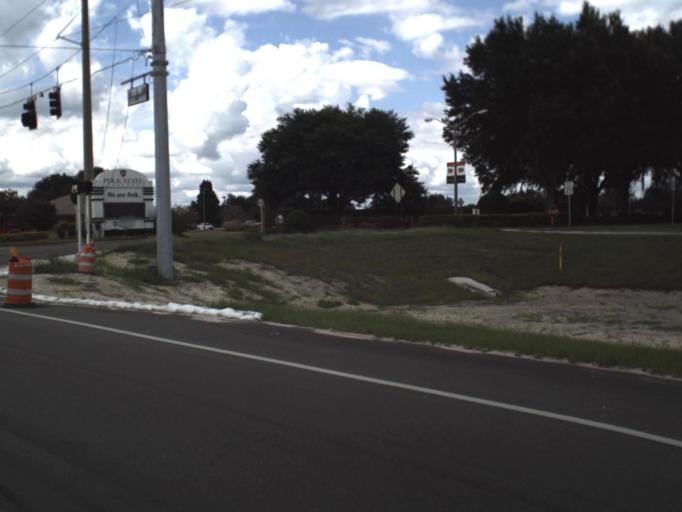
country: US
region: Florida
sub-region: Polk County
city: Highland City
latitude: 27.9893
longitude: -81.8941
